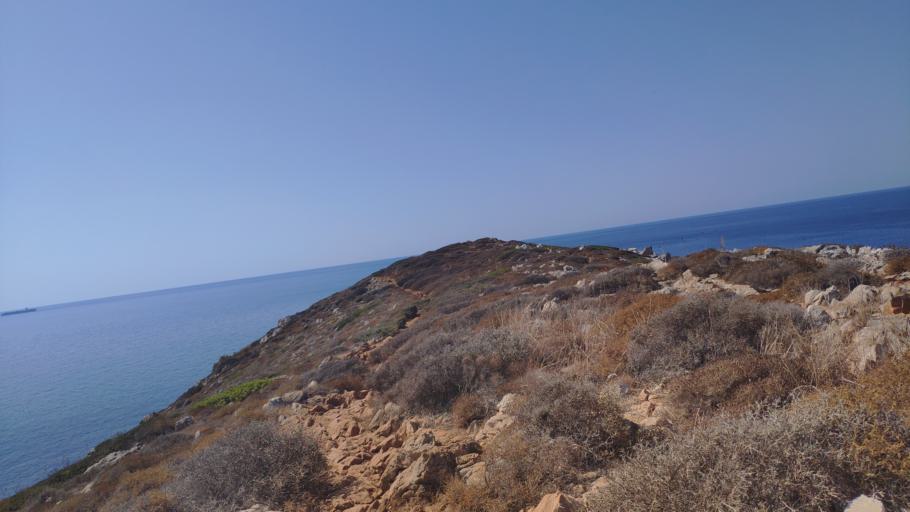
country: GR
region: Peloponnese
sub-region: Nomos Lakonias
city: Gytheio
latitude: 36.3892
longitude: 22.4825
